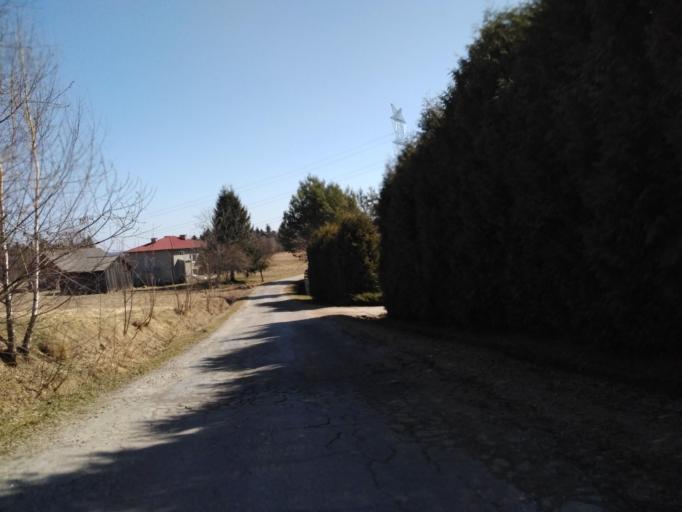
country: PL
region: Subcarpathian Voivodeship
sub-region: Powiat brzozowski
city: Jablonica Polska
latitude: 49.7359
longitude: 21.8965
